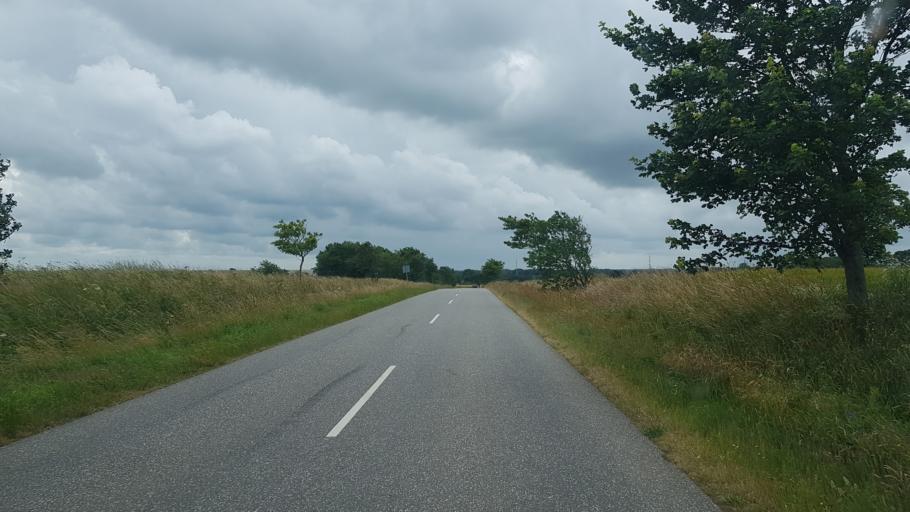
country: DK
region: South Denmark
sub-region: Kolding Kommune
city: Vamdrup
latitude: 55.4411
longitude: 9.2668
